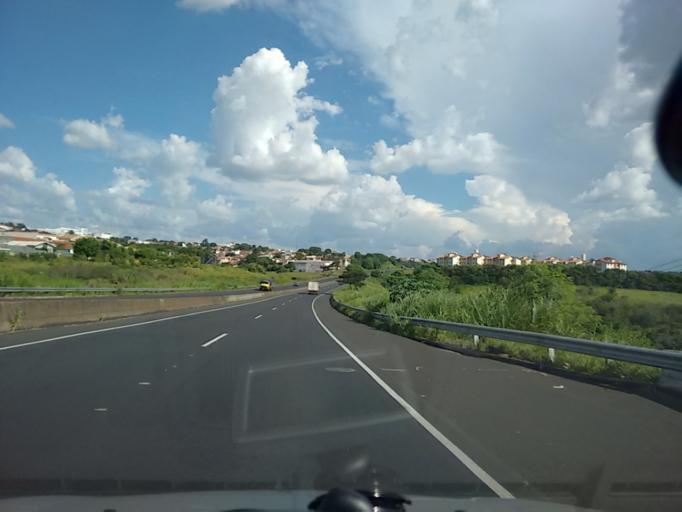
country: BR
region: Sao Paulo
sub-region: Marilia
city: Marilia
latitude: -22.1896
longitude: -49.9677
